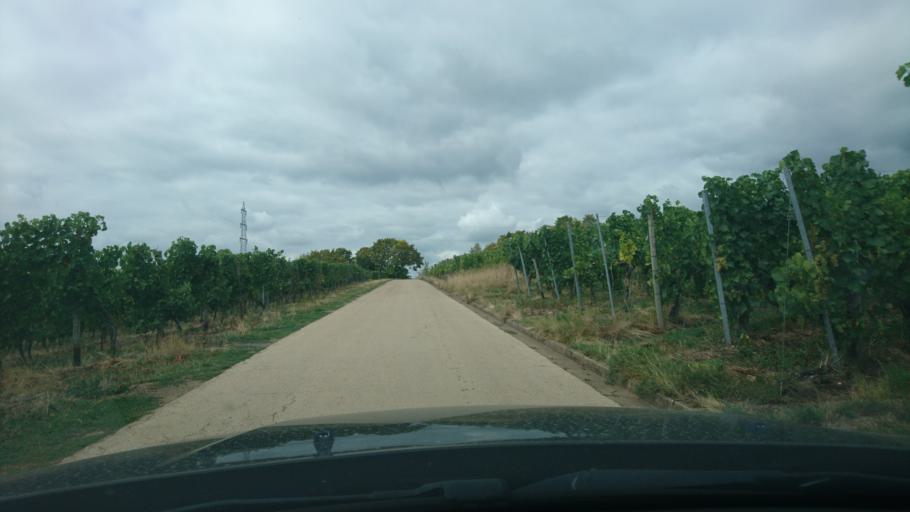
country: DE
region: Rheinland-Pfalz
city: Wiltingen
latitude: 49.6698
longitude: 6.6014
